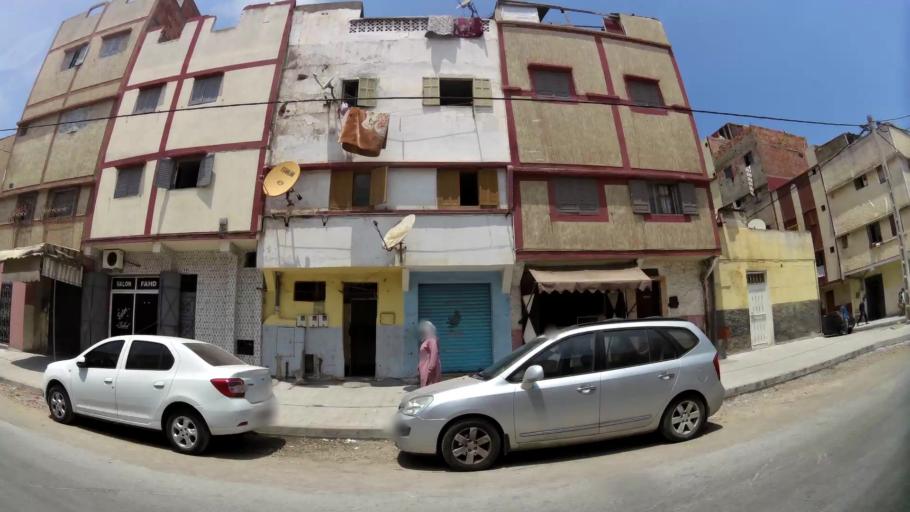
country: MA
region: Rabat-Sale-Zemmour-Zaer
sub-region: Rabat
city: Rabat
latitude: 33.9854
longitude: -6.8808
